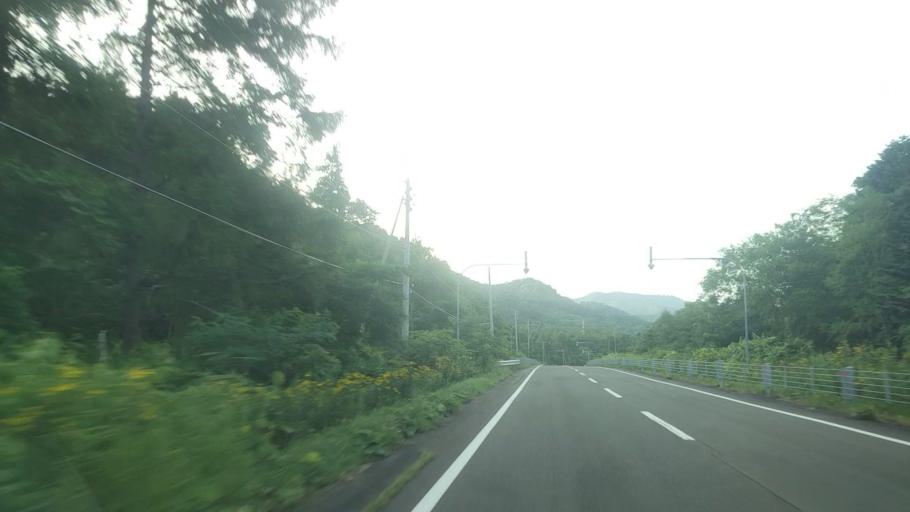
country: JP
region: Hokkaido
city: Bibai
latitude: 43.0797
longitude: 142.1007
